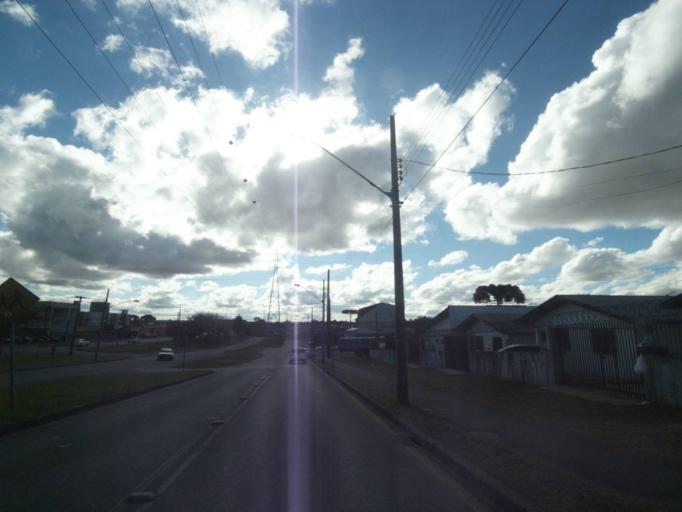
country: BR
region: Parana
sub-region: Sao Jose Dos Pinhais
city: Sao Jose dos Pinhais
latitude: -25.5300
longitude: -49.2887
